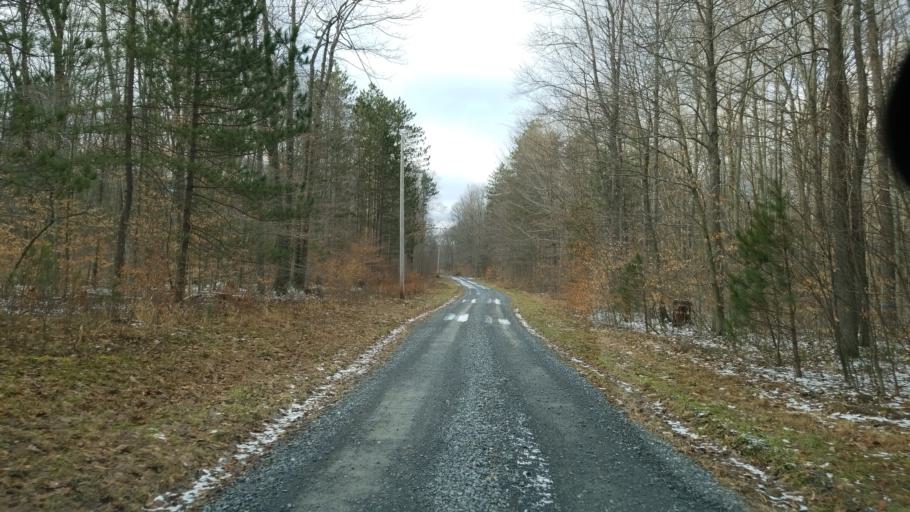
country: US
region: Pennsylvania
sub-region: Clearfield County
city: Clearfield
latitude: 41.1362
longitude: -78.5245
